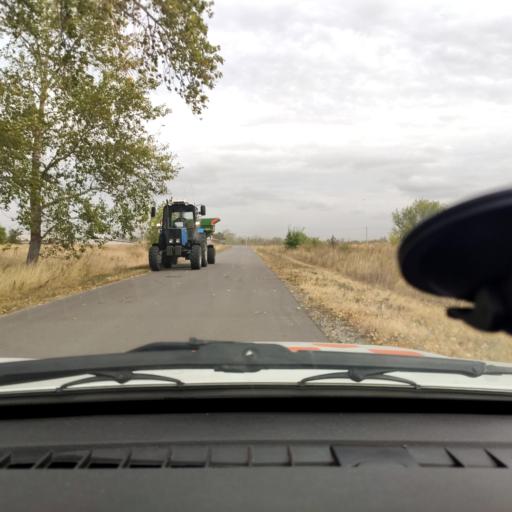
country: RU
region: Lipetsk
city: Khlevnoye
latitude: 52.0053
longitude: 39.1155
